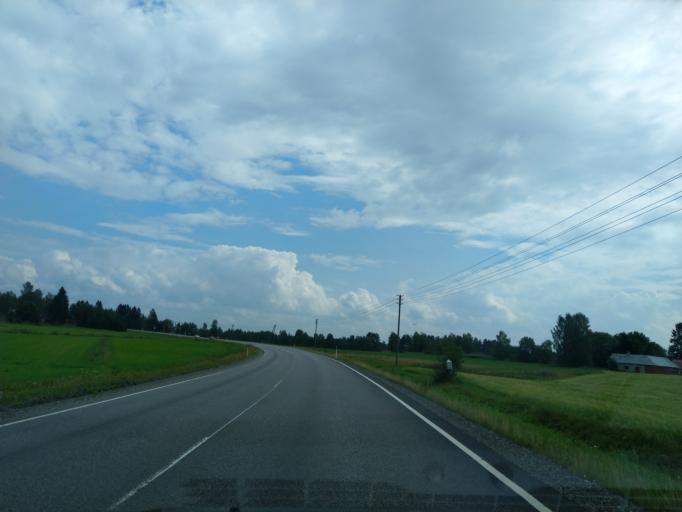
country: FI
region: South Karelia
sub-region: Imatra
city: Parikkala
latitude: 61.6056
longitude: 29.4633
